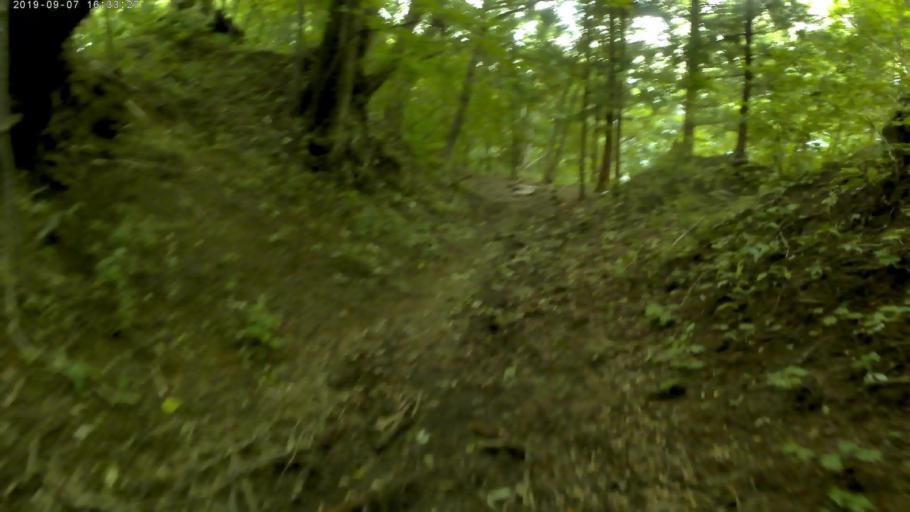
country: JP
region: Gunma
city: Annaka
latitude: 36.3636
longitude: 138.6926
